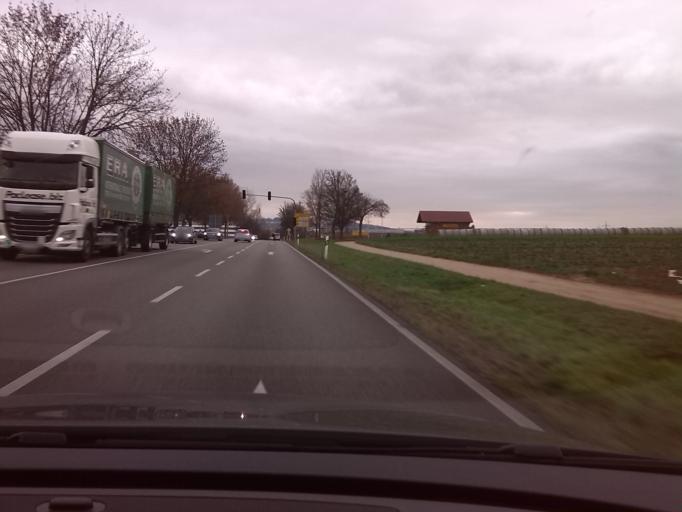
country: DE
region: Baden-Wuerttemberg
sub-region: Regierungsbezirk Stuttgart
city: Fellbach
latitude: 48.8240
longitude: 9.2561
